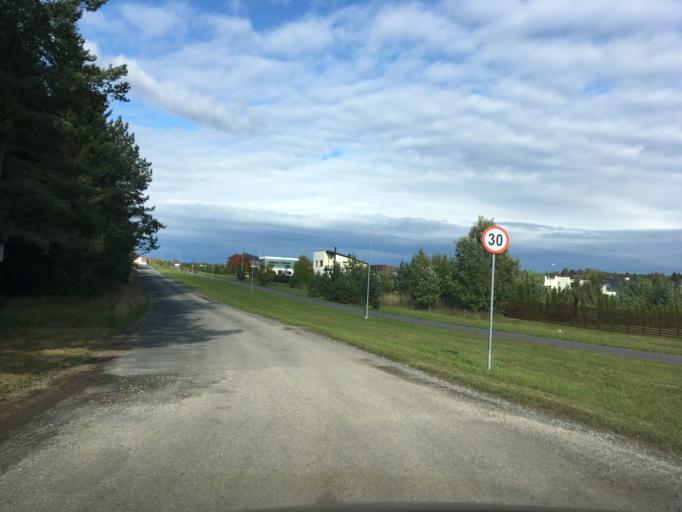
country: EE
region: Harju
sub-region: Saue vald
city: Laagri
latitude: 59.3418
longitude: 24.6496
